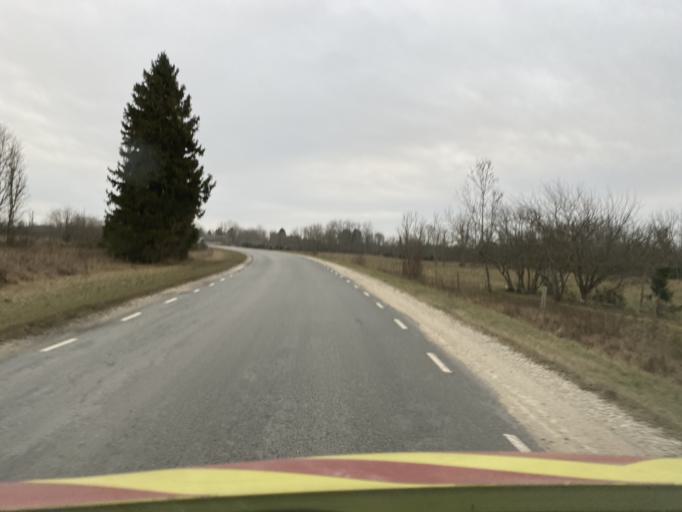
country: EE
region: Laeaene
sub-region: Ridala Parish
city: Uuemoisa
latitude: 59.0327
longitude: 23.6409
